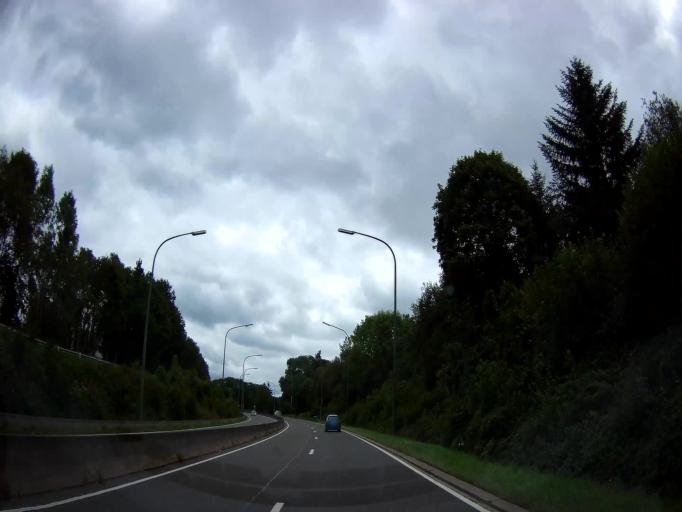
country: BE
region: Wallonia
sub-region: Province du Luxembourg
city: Marche-en-Famenne
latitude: 50.2190
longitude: 5.3436
